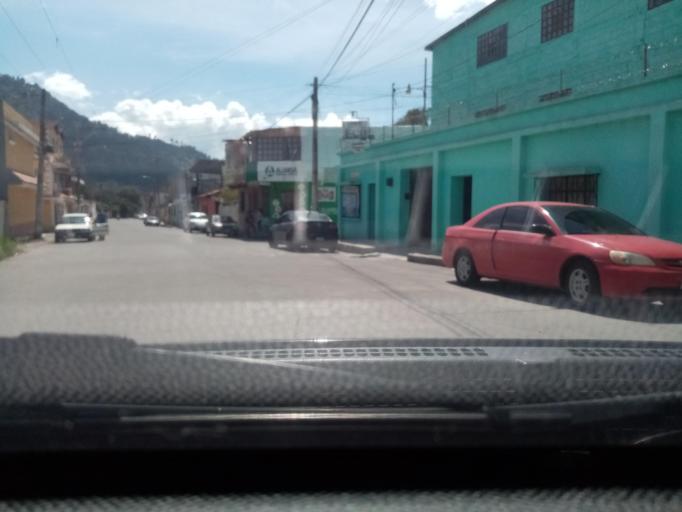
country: GT
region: Quetzaltenango
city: Quetzaltenango
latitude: 14.8401
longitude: -91.5124
